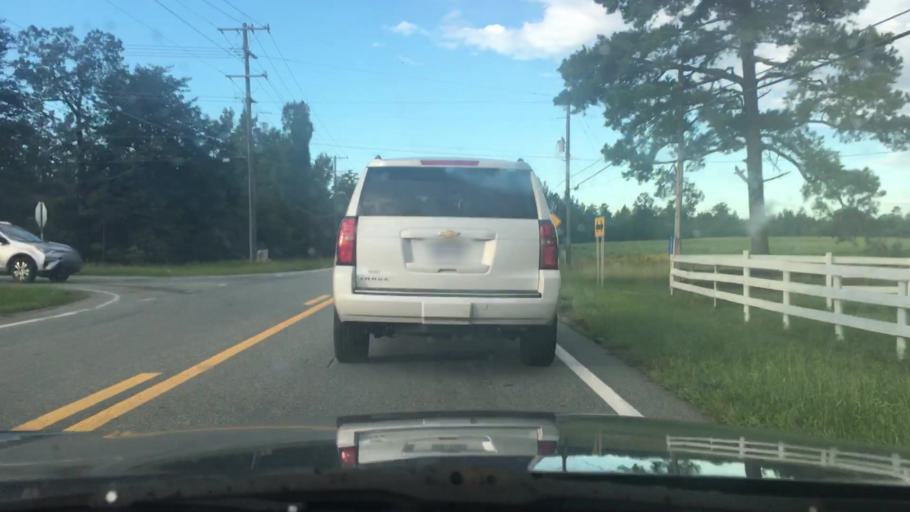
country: US
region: North Carolina
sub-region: Alamance County
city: Green Level
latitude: 36.1417
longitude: -79.3432
